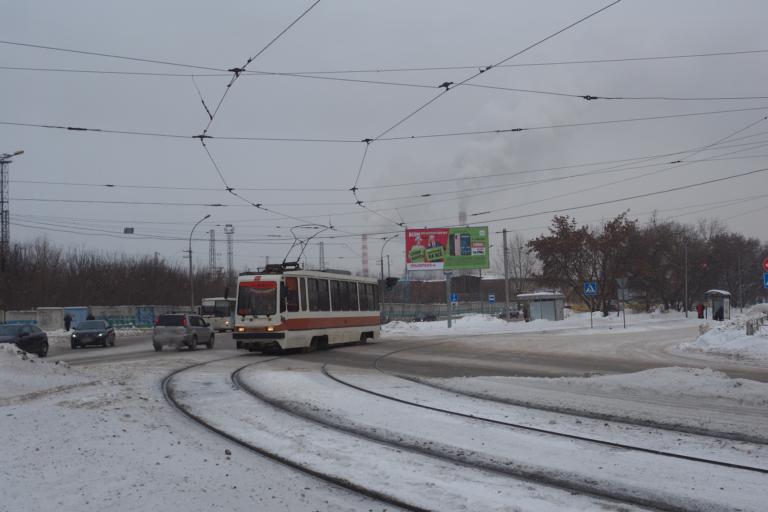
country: RU
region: Novosibirsk
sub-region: Novosibirskiy Rayon
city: Novosibirsk
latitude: 54.9939
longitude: 82.8569
